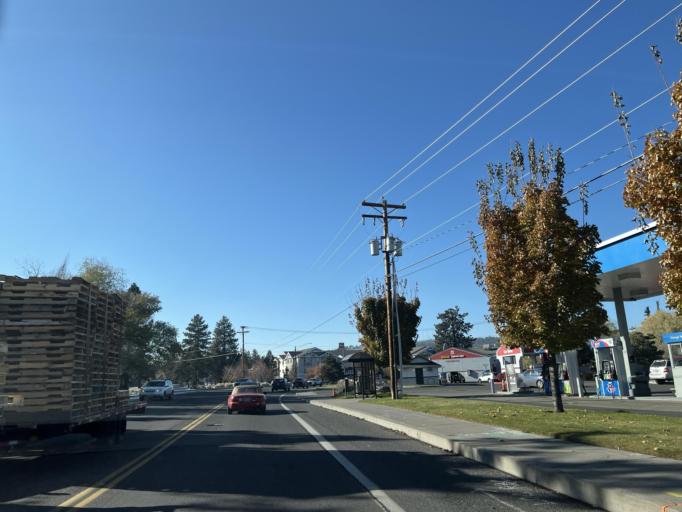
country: US
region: Oregon
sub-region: Deschutes County
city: Bend
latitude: 44.0764
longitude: -121.2957
